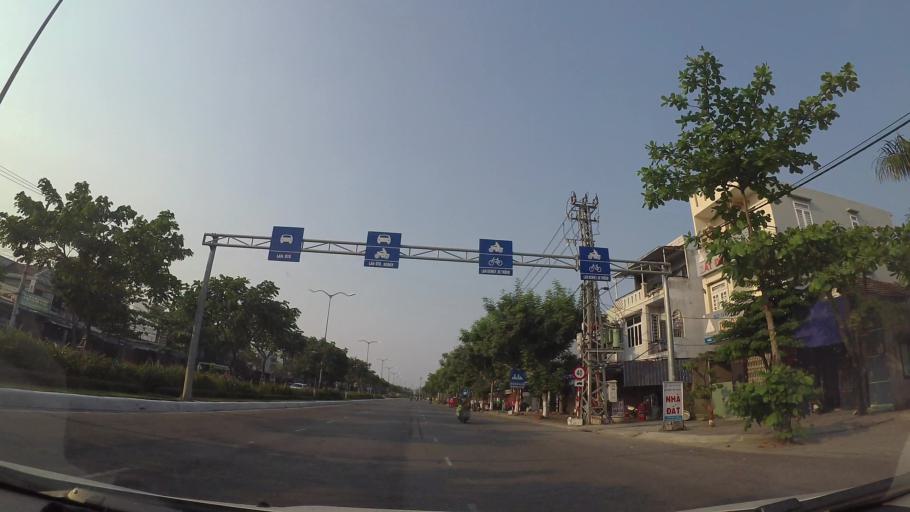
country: VN
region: Da Nang
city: Ngu Hanh Son
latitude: 15.9744
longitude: 108.2549
